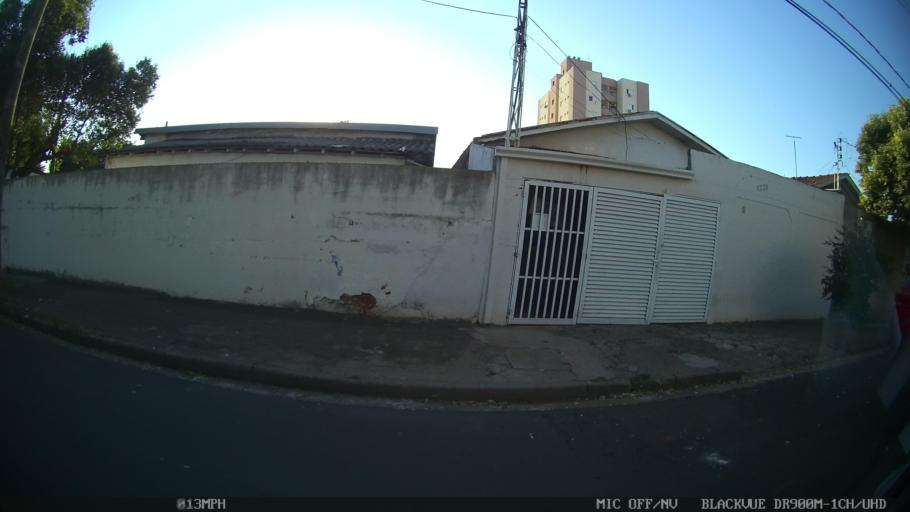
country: BR
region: Sao Paulo
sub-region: Sao Jose Do Rio Preto
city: Sao Jose do Rio Preto
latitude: -20.7969
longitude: -49.3898
